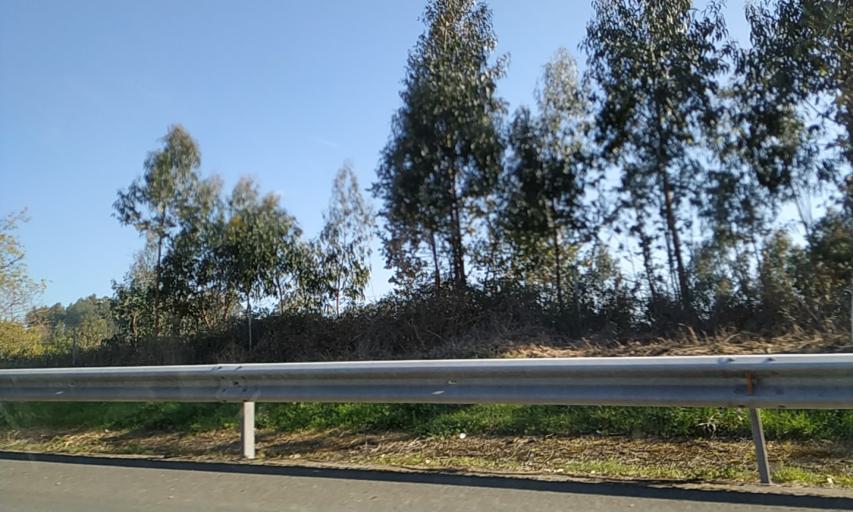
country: ES
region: Galicia
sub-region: Provincia da Coruna
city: Coiros
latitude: 43.2405
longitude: -8.1638
